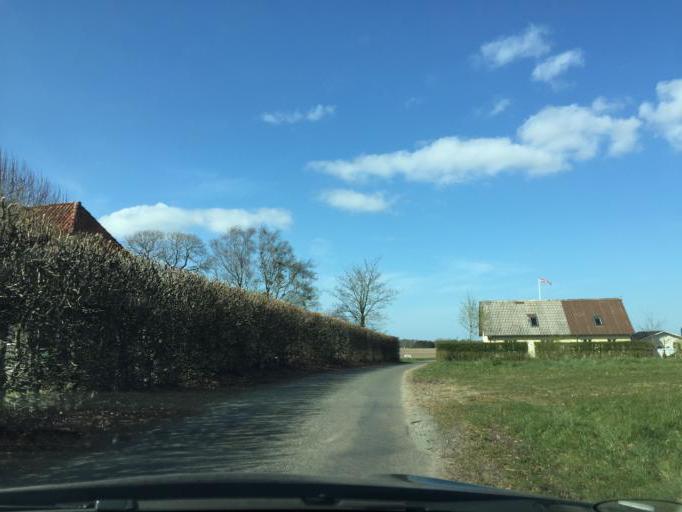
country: DK
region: South Denmark
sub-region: Faaborg-Midtfyn Kommune
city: Arslev
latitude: 55.2970
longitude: 10.5182
